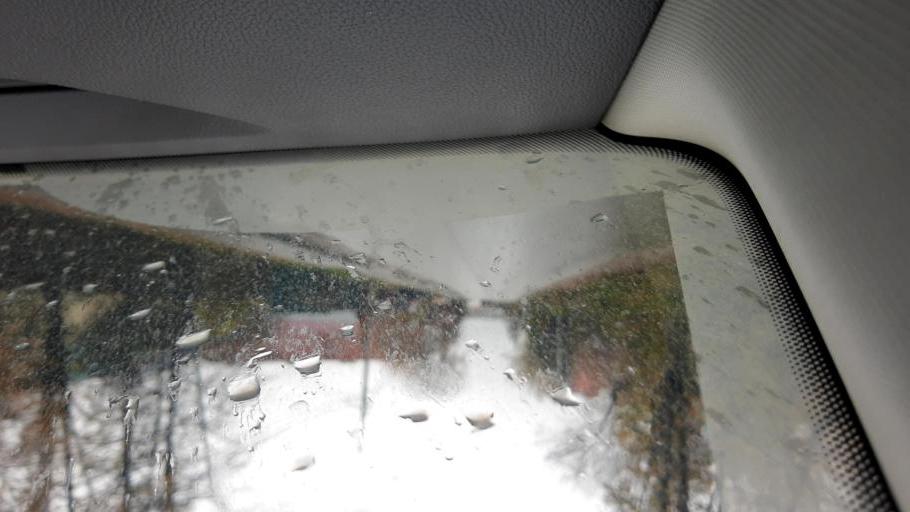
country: RU
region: Moskovskaya
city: Aprelevka
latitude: 55.5428
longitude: 37.0750
